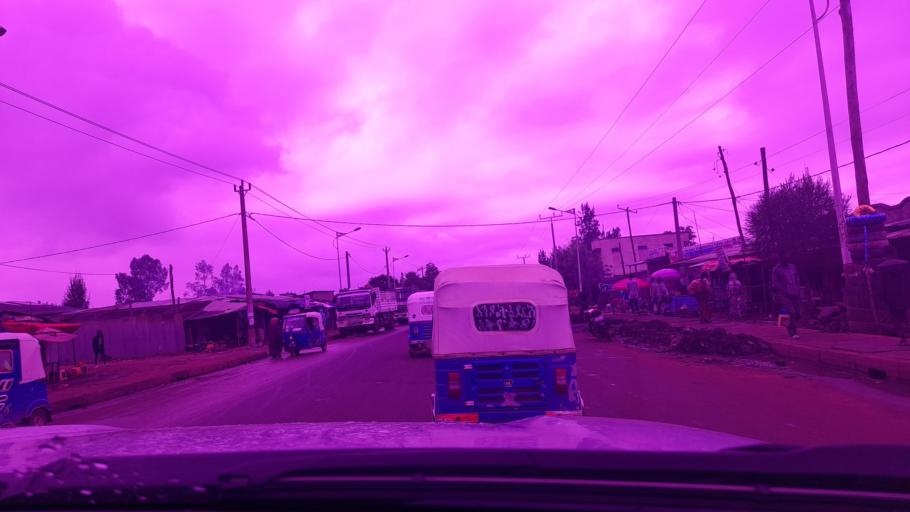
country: ET
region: Oromiya
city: Jima
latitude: 7.6590
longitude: 36.8431
